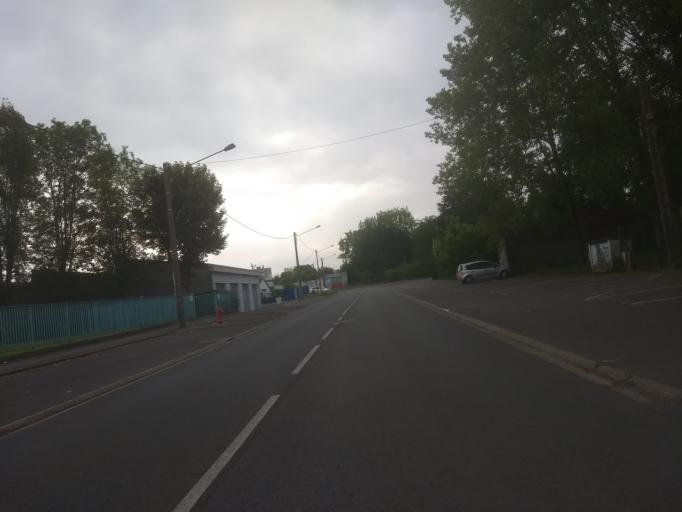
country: FR
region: Nord-Pas-de-Calais
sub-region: Departement du Pas-de-Calais
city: Dainville
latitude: 50.2969
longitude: 2.7353
